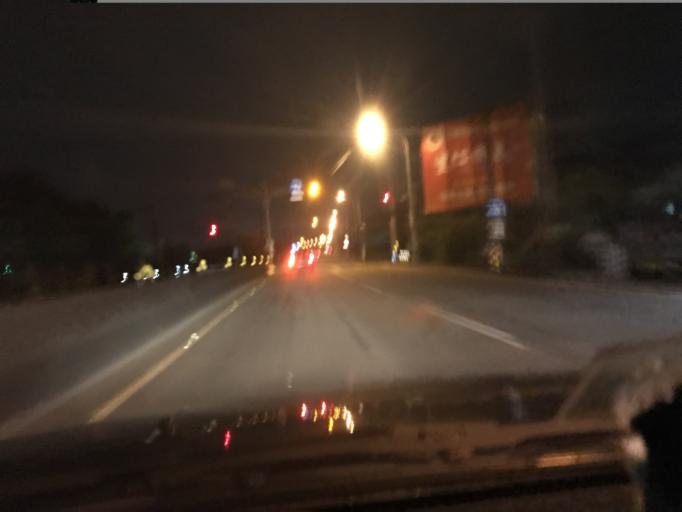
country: TW
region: Taiwan
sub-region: Hsinchu
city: Zhubei
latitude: 24.7815
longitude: 121.0690
